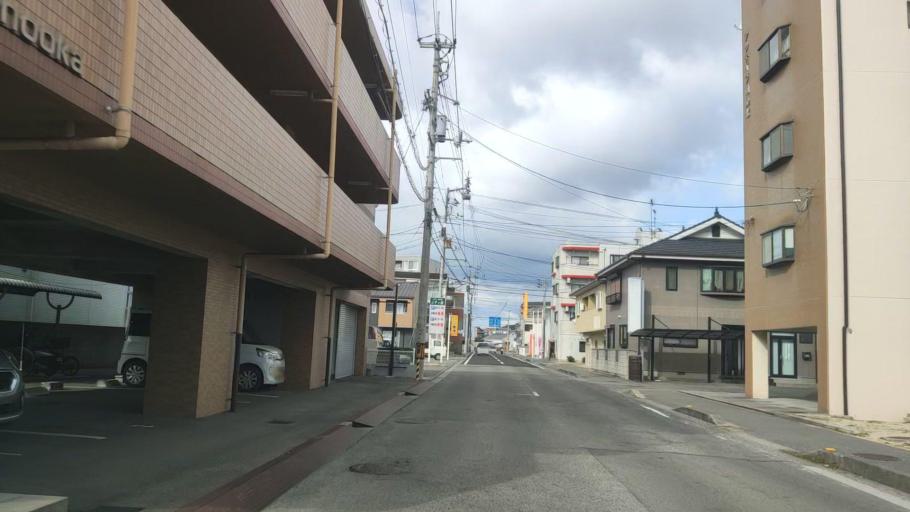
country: JP
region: Ehime
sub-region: Shikoku-chuo Shi
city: Matsuyama
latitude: 33.8220
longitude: 132.7586
